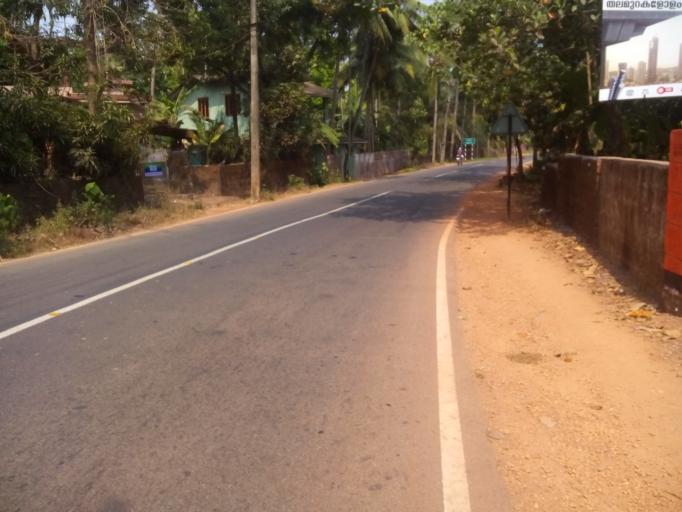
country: IN
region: Kerala
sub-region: Kozhikode
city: Naduvannur
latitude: 11.5838
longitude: 75.7632
